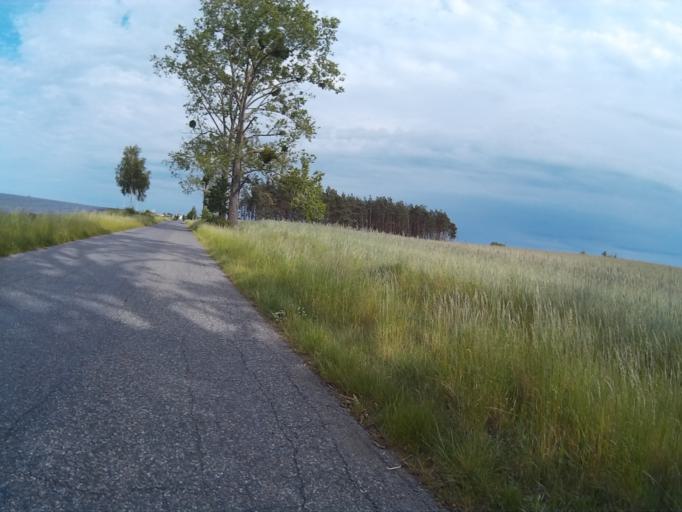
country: PL
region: Kujawsko-Pomorskie
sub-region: Powiat tucholski
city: Lubiewo
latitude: 53.4686
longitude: 17.9974
